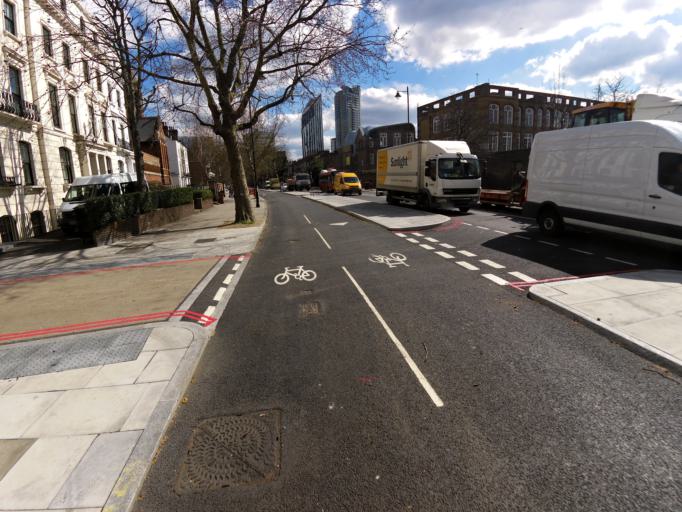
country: GB
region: England
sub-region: Greater London
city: Lambeth
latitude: 51.4968
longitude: -0.1062
